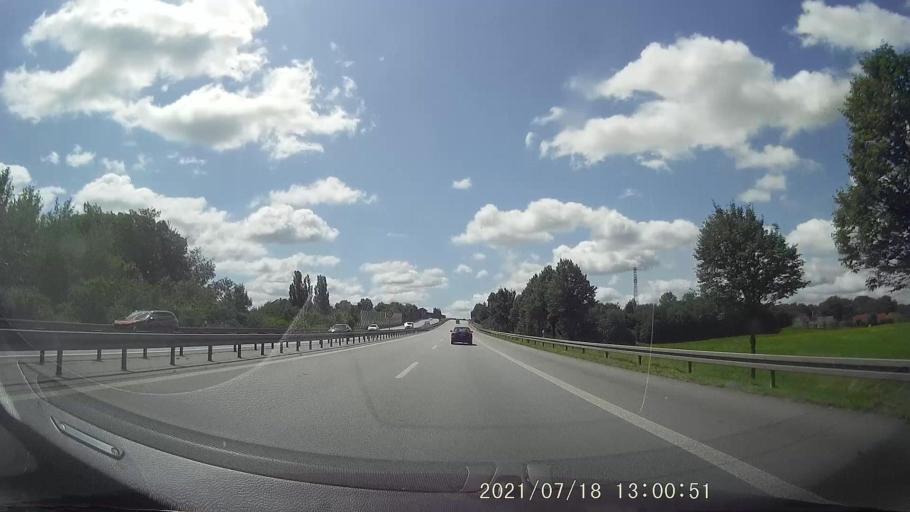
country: DE
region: Saxony
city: Bautzen
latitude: 51.1923
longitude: 14.4191
